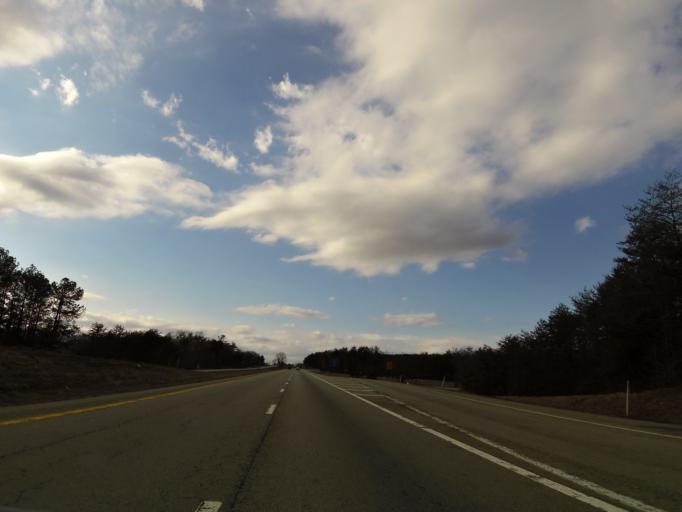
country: US
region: Tennessee
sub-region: Cumberland County
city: Fairfield Glade
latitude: 35.9273
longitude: -84.9146
